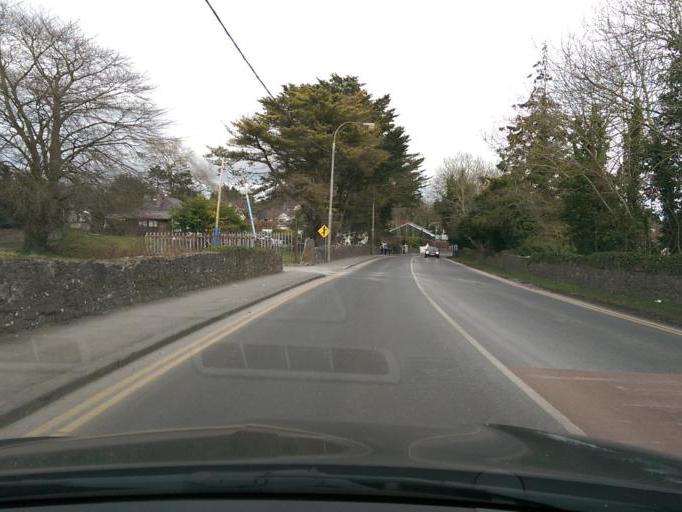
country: IE
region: Leinster
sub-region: An Iarmhi
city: Athlone
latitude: 53.4194
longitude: -7.9180
